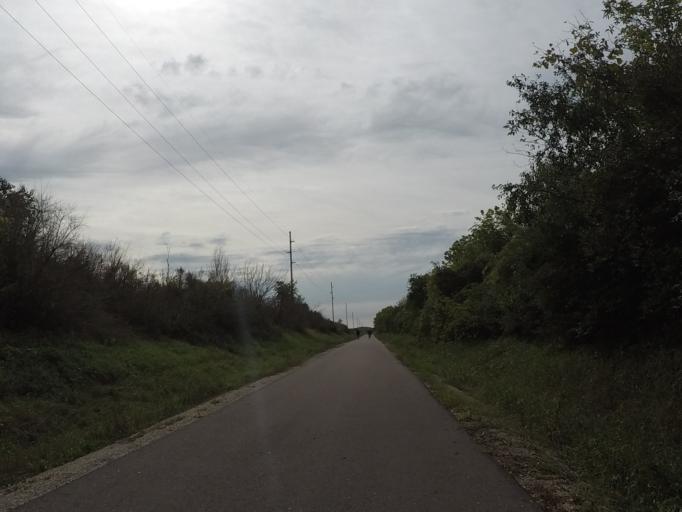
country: US
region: Wisconsin
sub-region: Sauk County
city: Prairie du Sac
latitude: 43.3256
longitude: -89.7463
